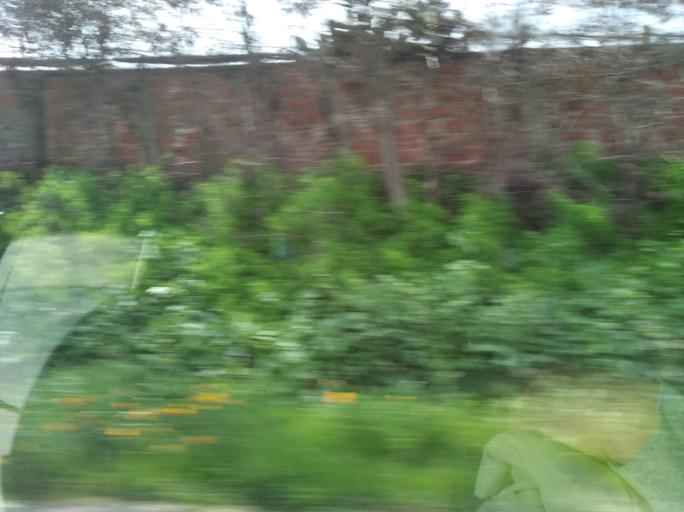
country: CL
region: Valparaiso
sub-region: Provincia de Marga Marga
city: Limache
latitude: -32.9716
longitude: -71.2832
